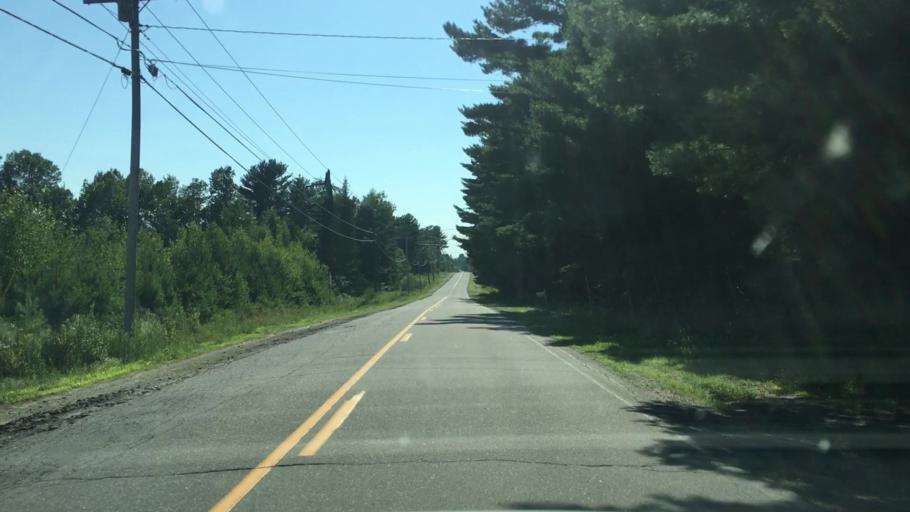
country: US
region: Maine
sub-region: Penobscot County
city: Enfield
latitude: 45.2467
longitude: -68.5983
